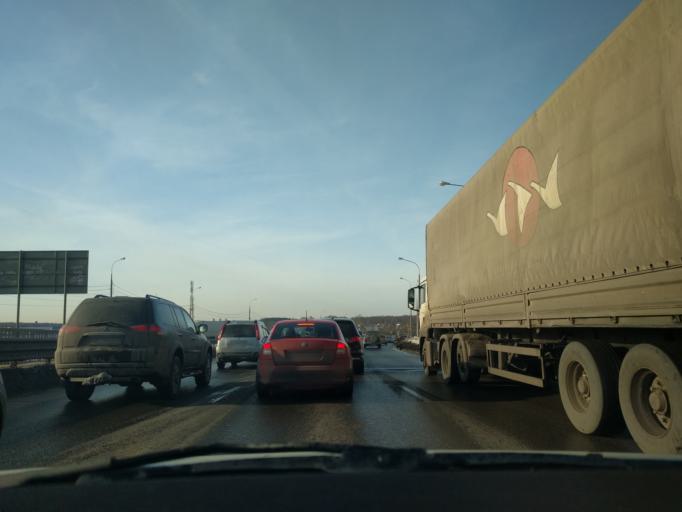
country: RU
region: Moskovskaya
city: Sheremet'yevskiy
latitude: 55.9737
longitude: 37.5265
